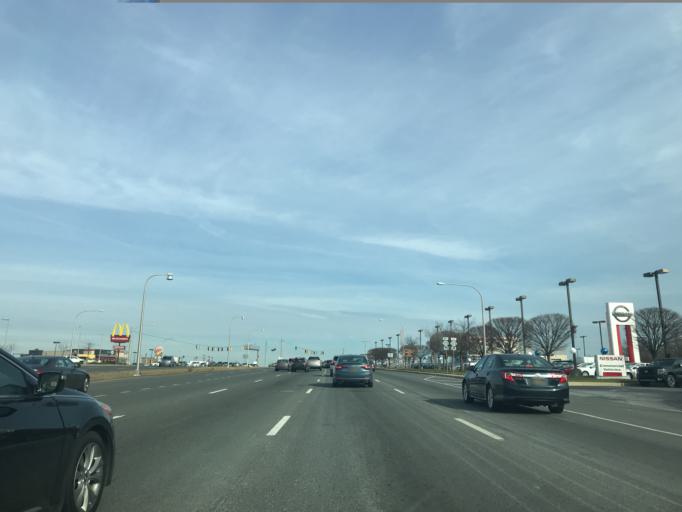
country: US
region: Delaware
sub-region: New Castle County
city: Wilmington Manor
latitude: 39.6646
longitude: -75.6047
